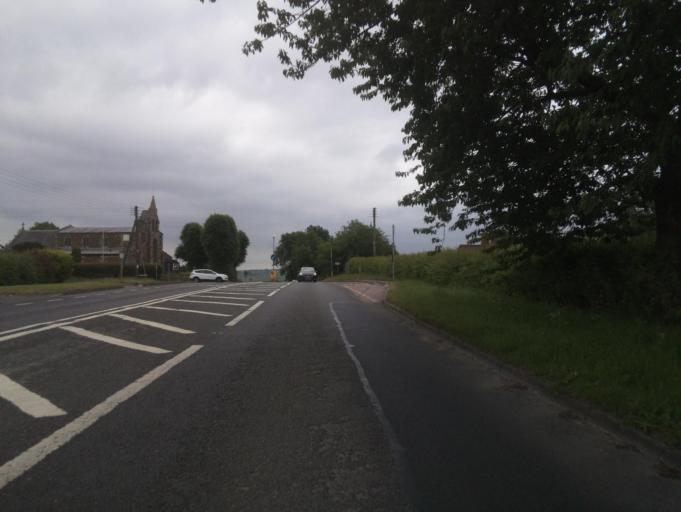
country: GB
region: England
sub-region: Leicestershire
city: Melton Mowbray
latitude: 52.7452
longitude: -0.8654
